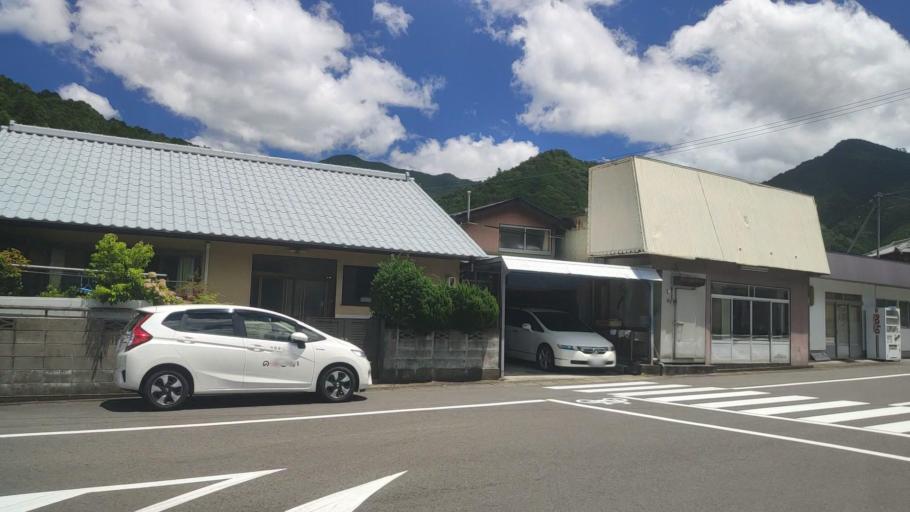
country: JP
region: Mie
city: Owase
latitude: 33.9841
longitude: 136.0402
